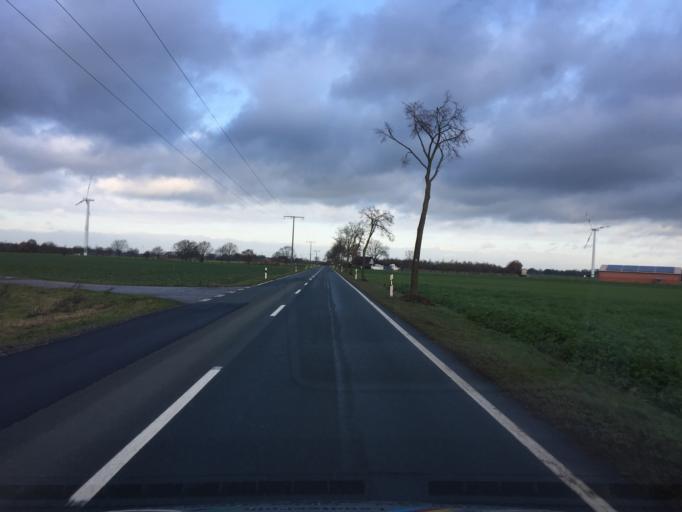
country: DE
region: Lower Saxony
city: Raddestorf
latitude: 52.4841
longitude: 8.9991
